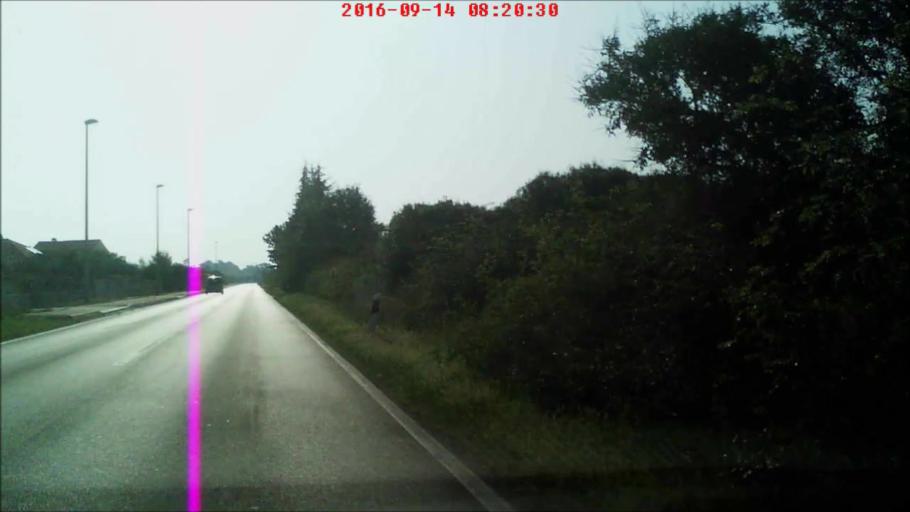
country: HR
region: Zadarska
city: Nin
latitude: 44.2263
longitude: 15.2011
